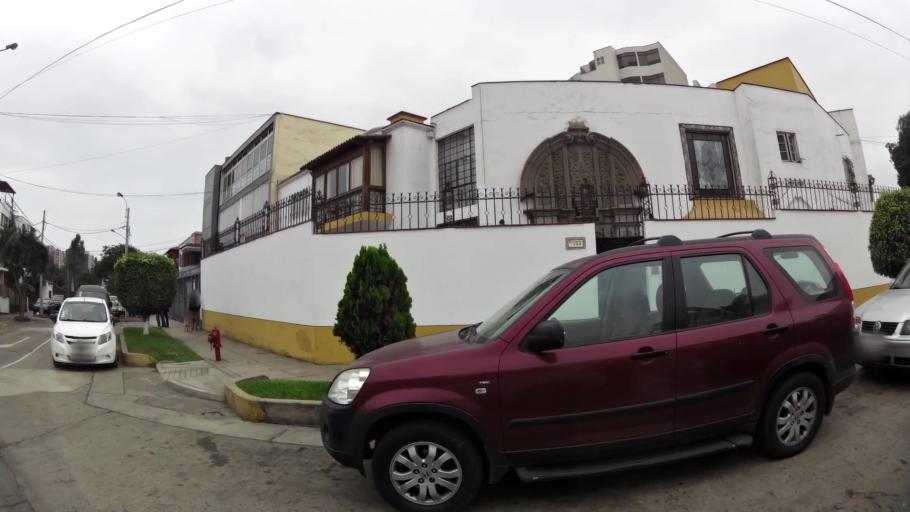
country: PE
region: Lima
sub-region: Lima
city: Surco
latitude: -12.1248
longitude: -77.0212
